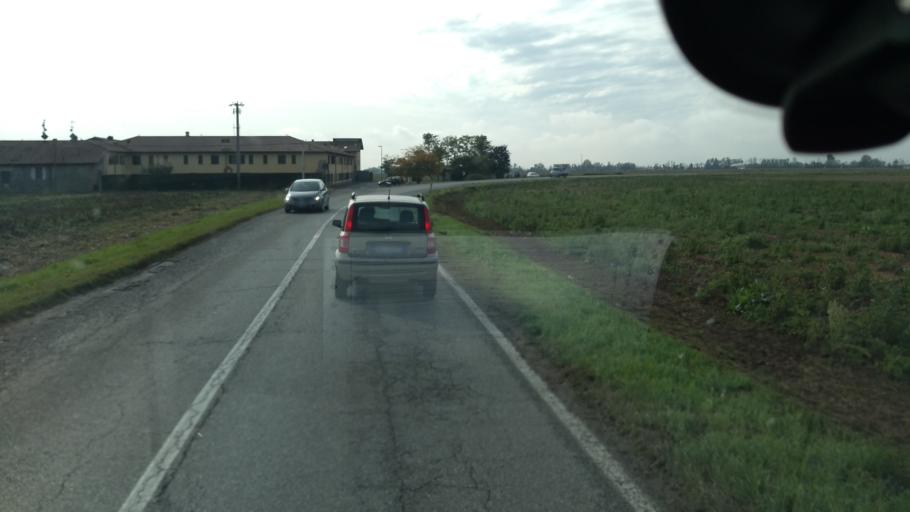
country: IT
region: Lombardy
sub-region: Provincia di Bergamo
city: Cologno al Serio
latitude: 45.5639
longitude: 9.6931
